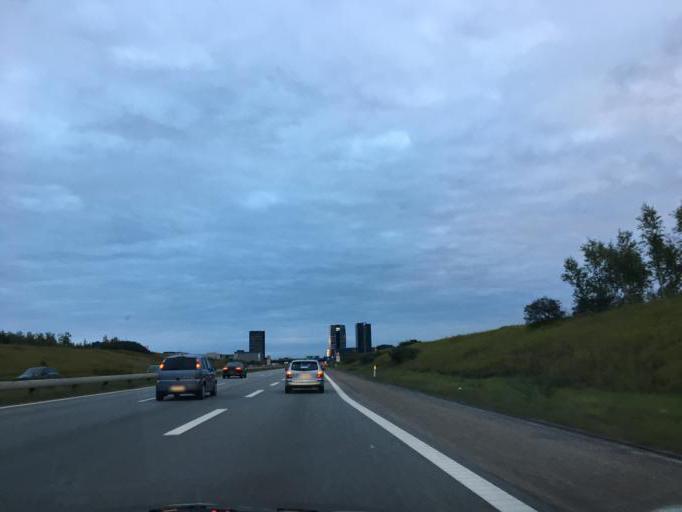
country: DK
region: Capital Region
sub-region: Tarnby Kommune
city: Tarnby
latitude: 55.6290
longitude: 12.5573
